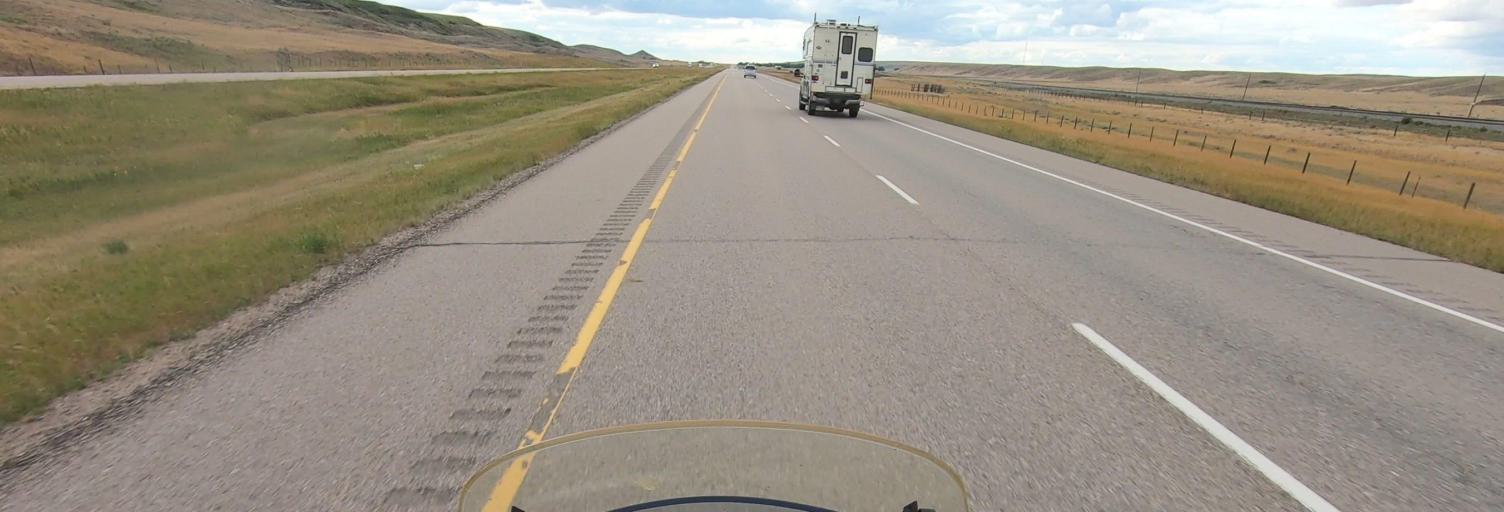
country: CA
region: Alberta
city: Medicine Hat
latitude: 49.9508
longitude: -110.2330
